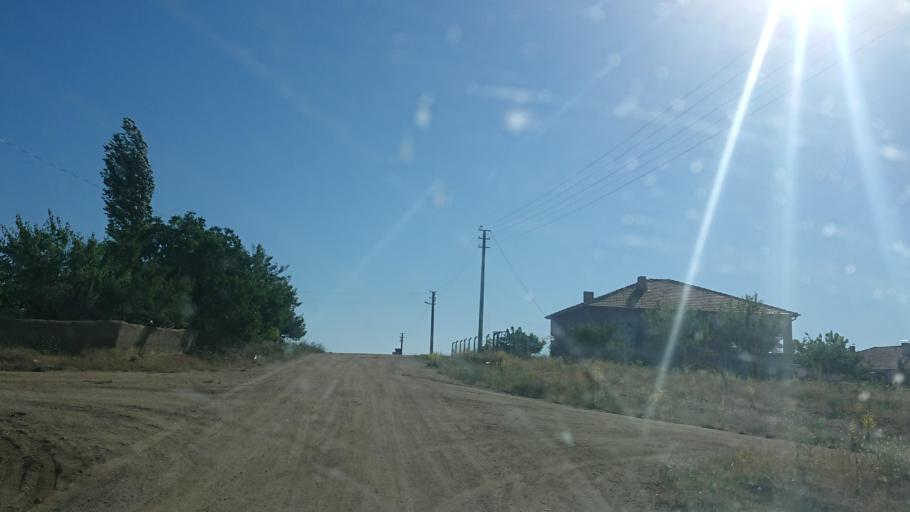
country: TR
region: Aksaray
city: Agacoren
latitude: 38.8733
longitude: 33.9471
